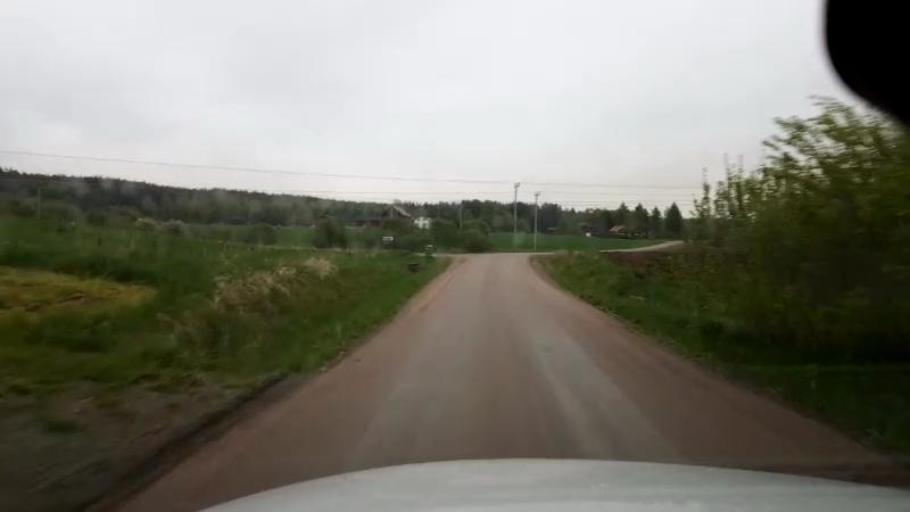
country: SE
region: Gaevleborg
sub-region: Ljusdals Kommun
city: Jaervsoe
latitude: 61.7558
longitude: 16.1787
